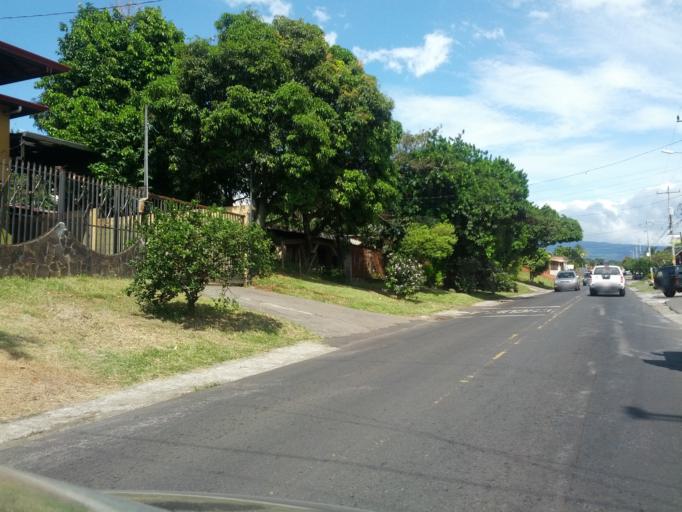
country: CR
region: Alajuela
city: Alajuela
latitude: 10.0233
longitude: -84.1882
